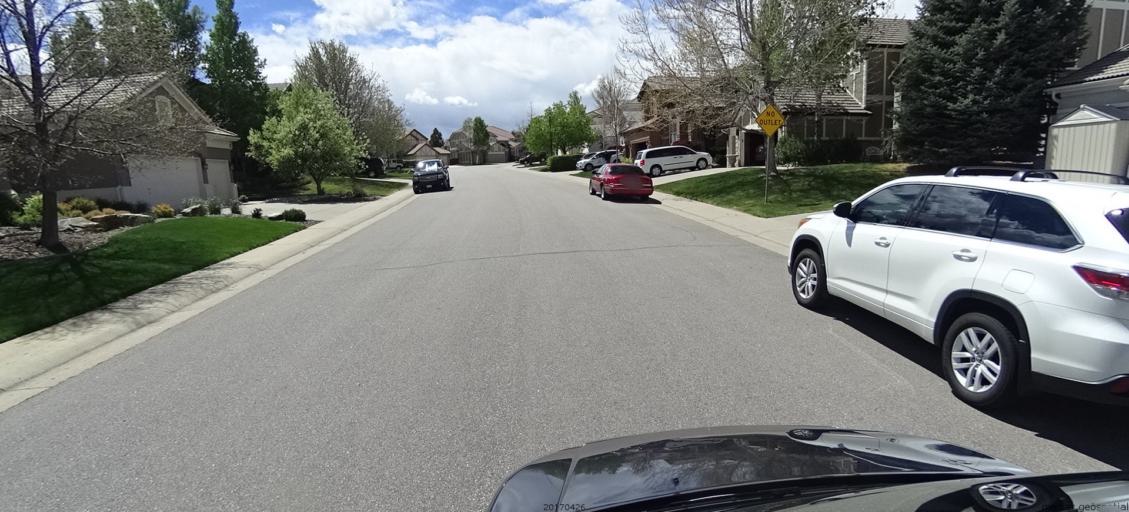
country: US
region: Colorado
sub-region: Adams County
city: Lone Tree
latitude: 39.5401
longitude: -104.8898
